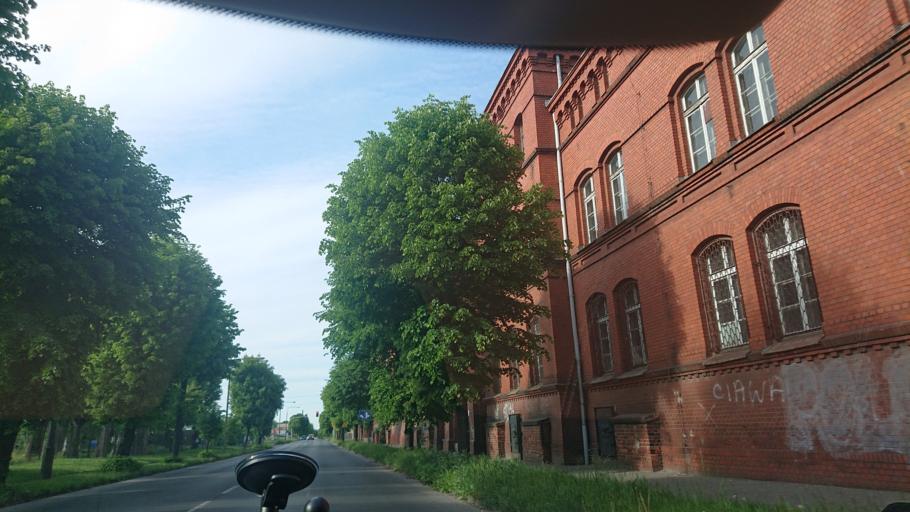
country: PL
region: Greater Poland Voivodeship
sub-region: Powiat gnieznienski
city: Gniezno
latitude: 52.5170
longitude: 17.5954
